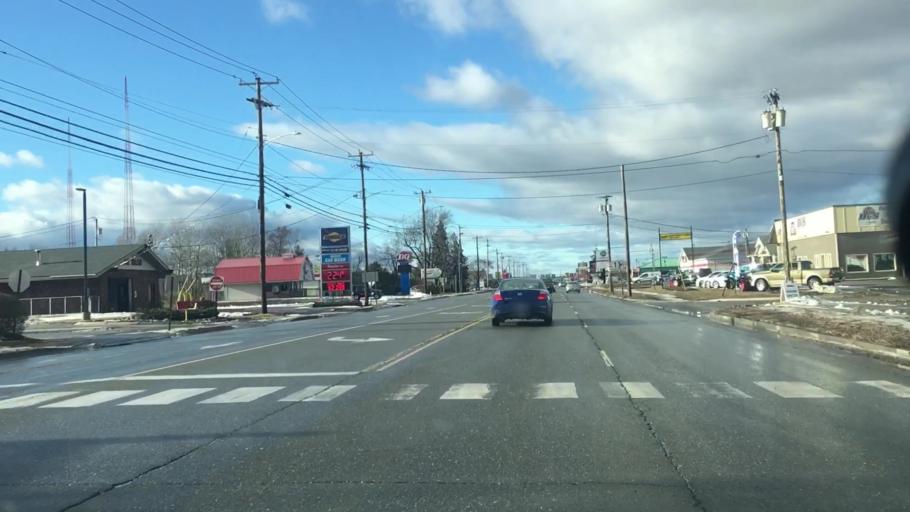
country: US
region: Maine
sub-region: Penobscot County
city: Brewer
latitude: 44.7806
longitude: -68.7430
